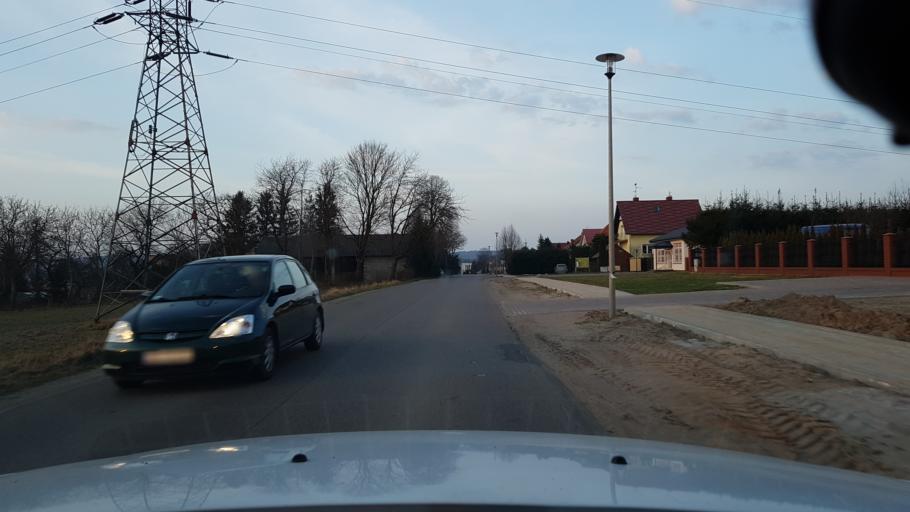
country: PL
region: West Pomeranian Voivodeship
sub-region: Koszalin
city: Koszalin
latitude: 54.1566
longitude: 16.2118
